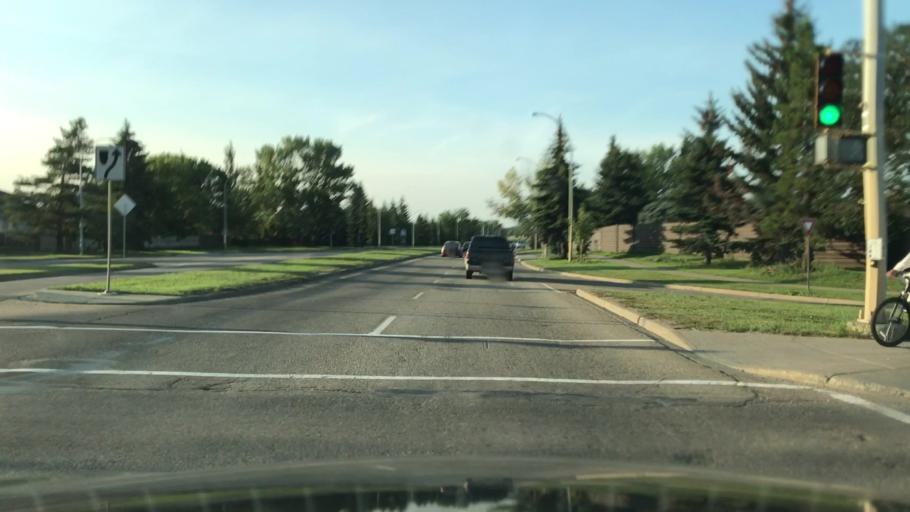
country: CA
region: Alberta
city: Beaumont
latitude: 53.4457
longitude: -113.4193
